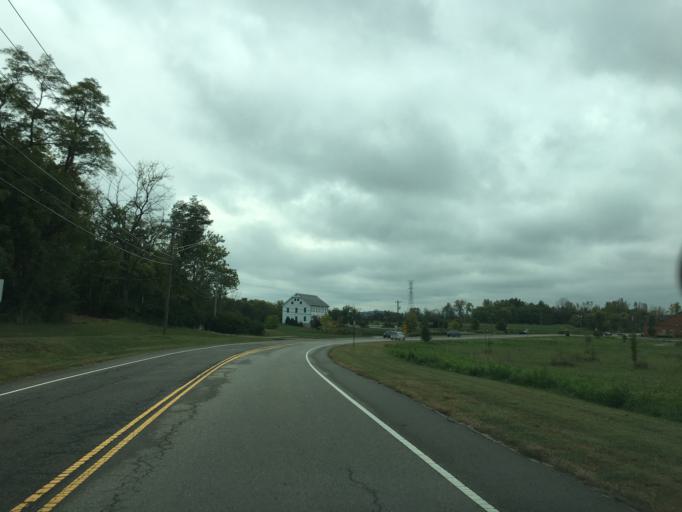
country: US
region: Ohio
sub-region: Butler County
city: Beckett Ridge
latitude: 39.3451
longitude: -84.4446
